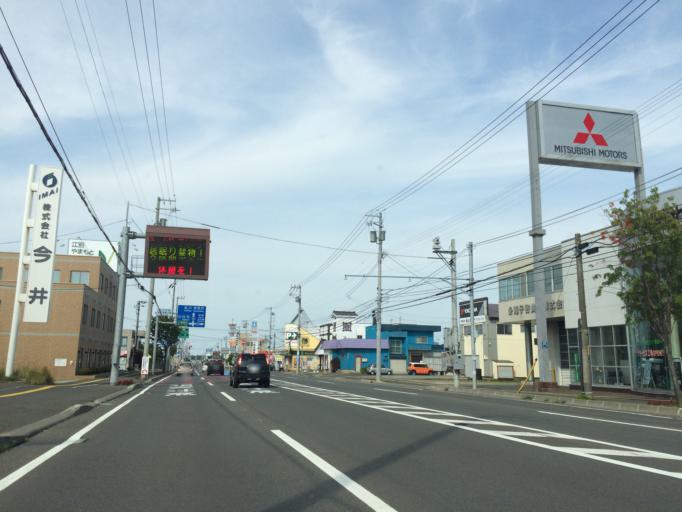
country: JP
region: Hokkaido
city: Ebetsu
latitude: 43.1044
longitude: 141.5396
